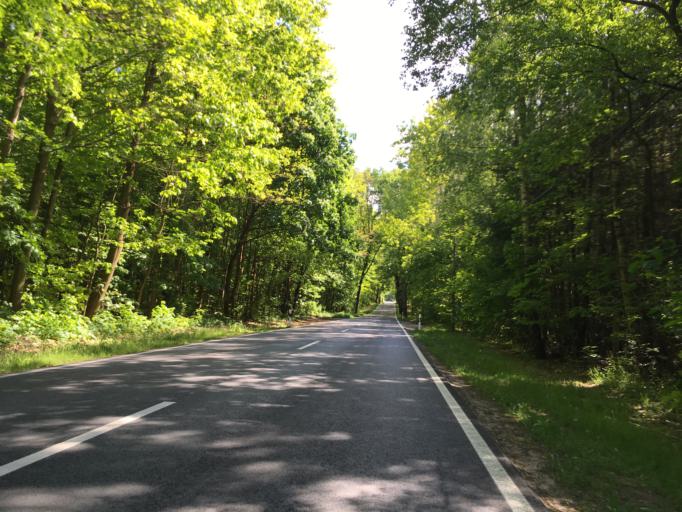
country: DE
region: Brandenburg
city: Bernau bei Berlin
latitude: 52.6292
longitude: 13.6117
